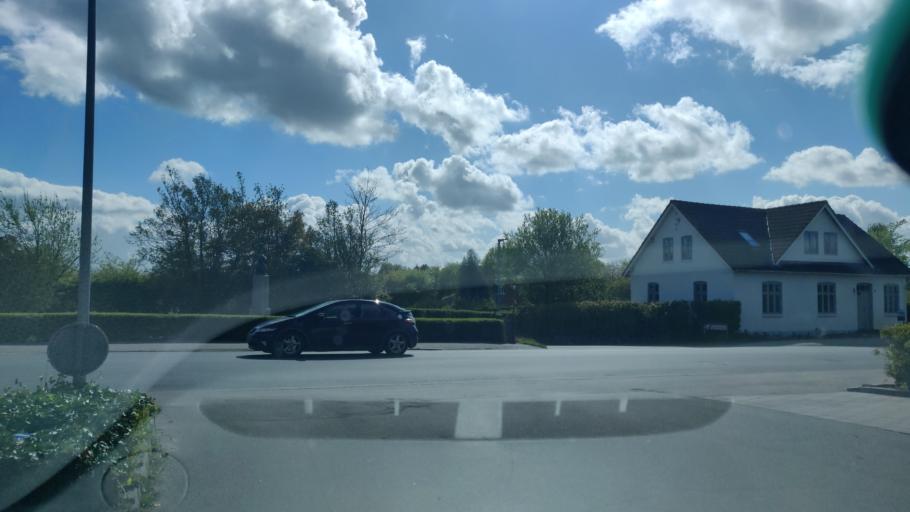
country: DK
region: South Denmark
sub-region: Kolding Kommune
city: Kolding
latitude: 55.5651
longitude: 9.4051
